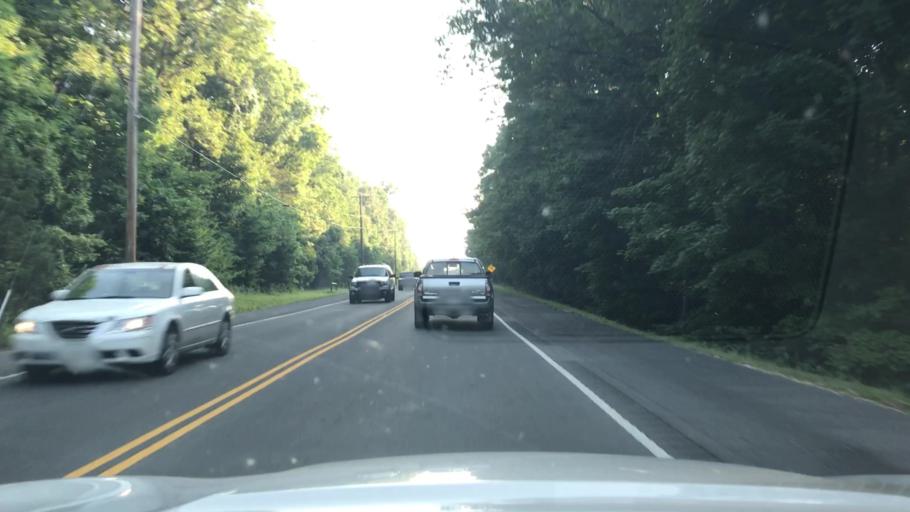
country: US
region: Tennessee
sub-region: Rutherford County
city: La Vergne
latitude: 36.0906
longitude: -86.5603
